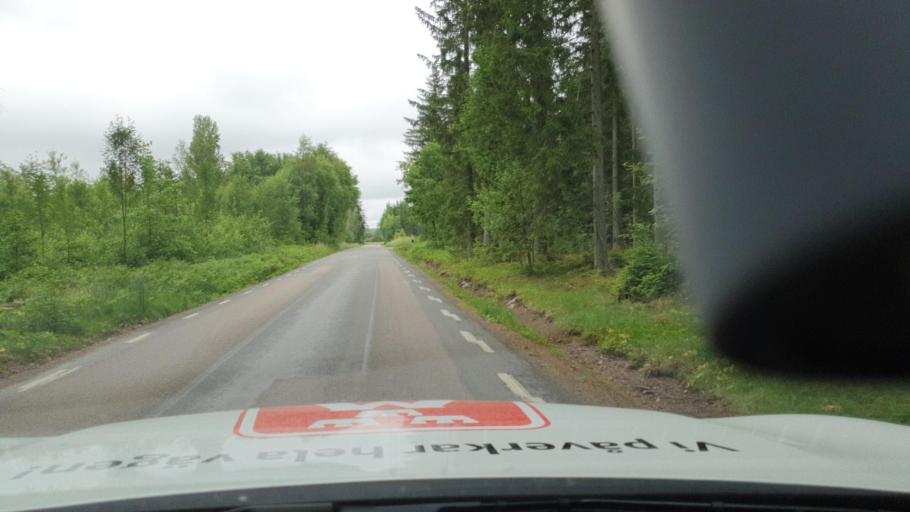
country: SE
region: Vaestra Goetaland
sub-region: Tibro Kommun
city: Tibro
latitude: 58.3773
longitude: 14.0513
